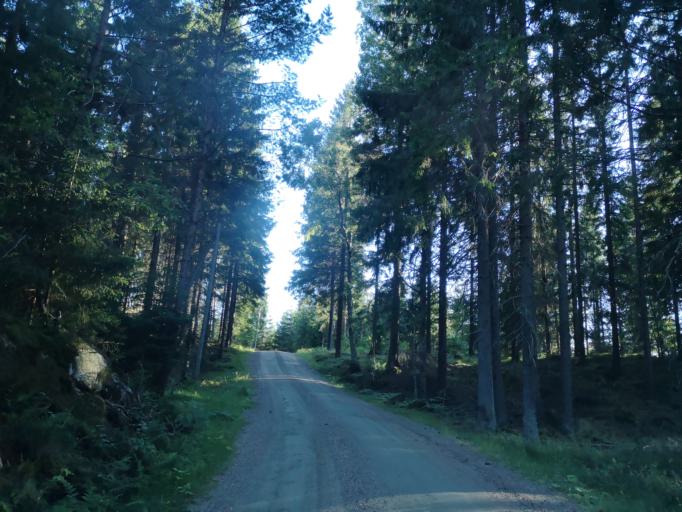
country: SE
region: Vaestra Goetaland
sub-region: Alingsas Kommun
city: Alingsas
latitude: 58.0206
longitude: 12.5552
